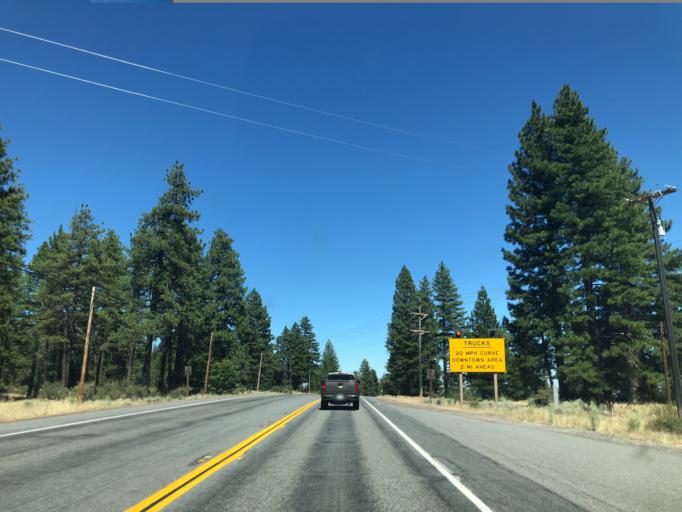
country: US
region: California
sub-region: Lassen County
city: Susanville
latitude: 40.4223
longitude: -120.6958
